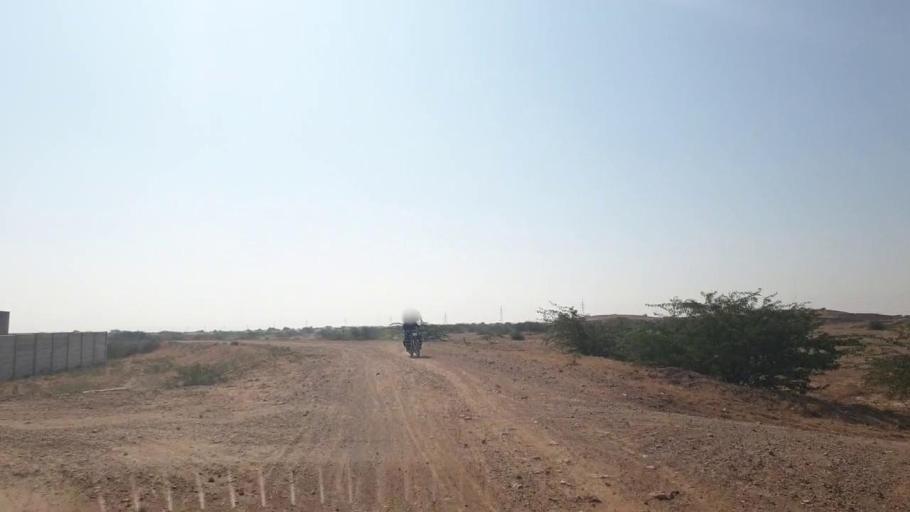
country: PK
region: Sindh
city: Gharo
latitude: 25.1438
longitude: 67.7271
